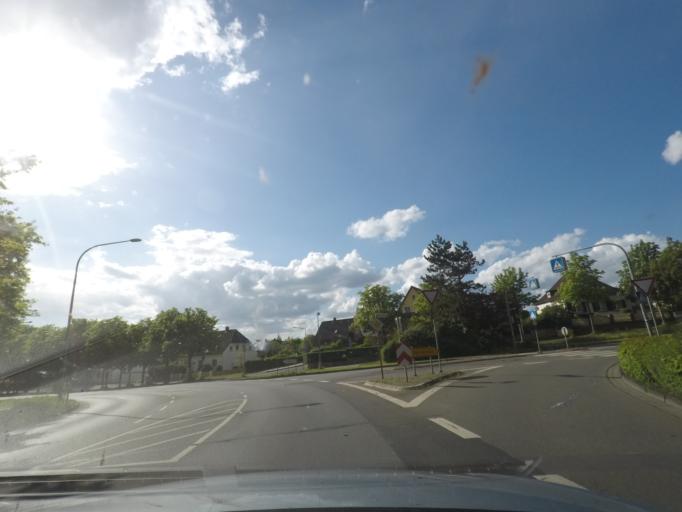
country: DE
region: Lower Saxony
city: Helmstedt
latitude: 52.2286
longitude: 11.0270
